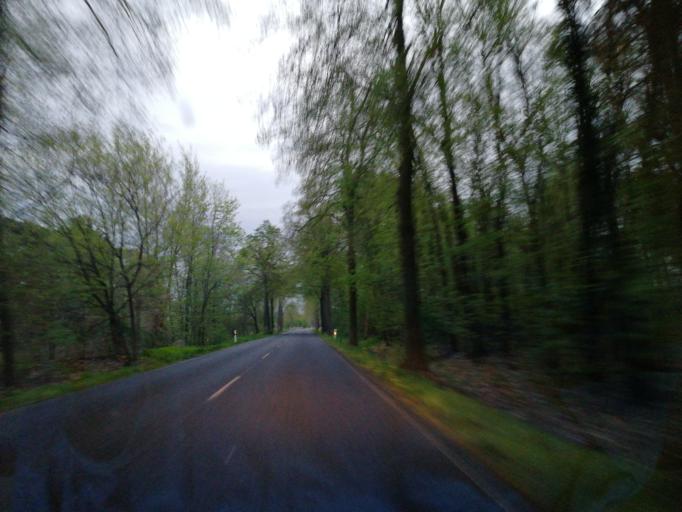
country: DE
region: Brandenburg
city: Calau
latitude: 51.7532
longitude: 13.9327
